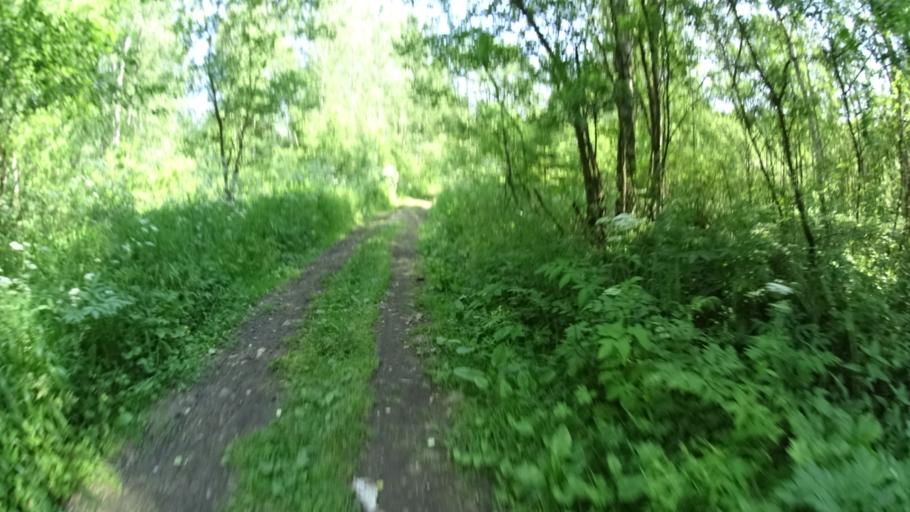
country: RU
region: Moskovskaya
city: Lesnoy
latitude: 56.0801
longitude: 37.9498
